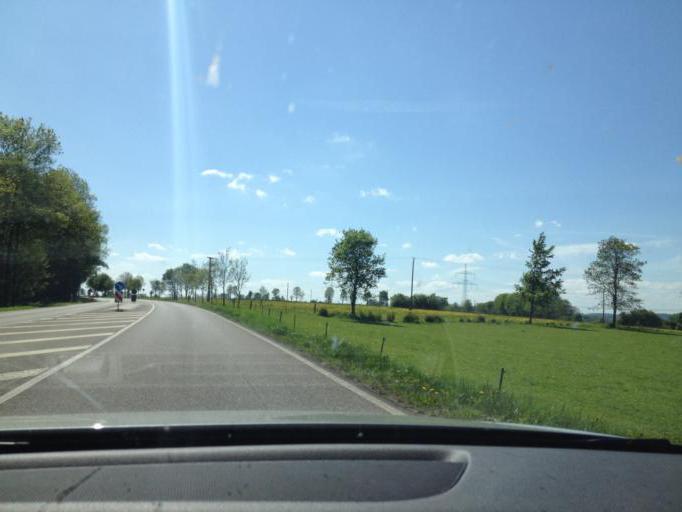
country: DE
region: North Rhine-Westphalia
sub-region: Regierungsbezirk Koln
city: Dahlem
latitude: 50.4149
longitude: 6.5805
